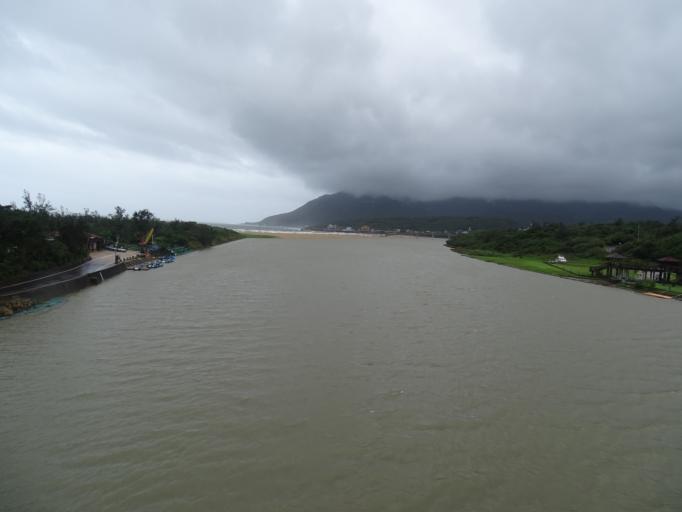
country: TW
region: Taiwan
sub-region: Keelung
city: Keelung
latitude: 25.0228
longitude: 121.9356
